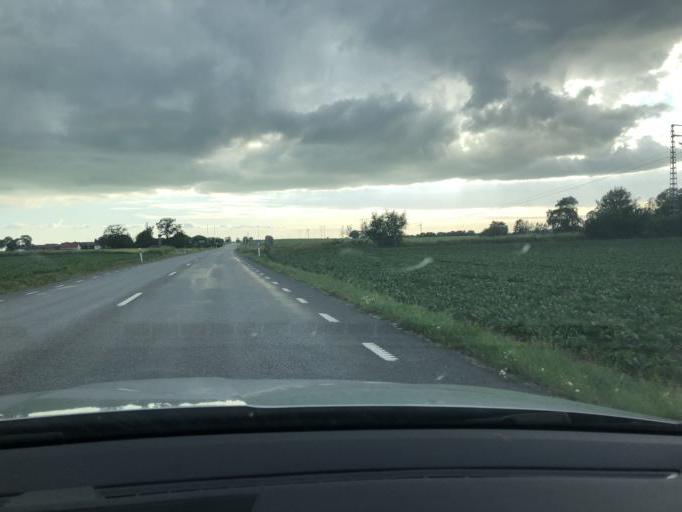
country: SE
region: Skane
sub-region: Simrishamns Kommun
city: Simrishamn
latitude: 55.5280
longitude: 14.2429
